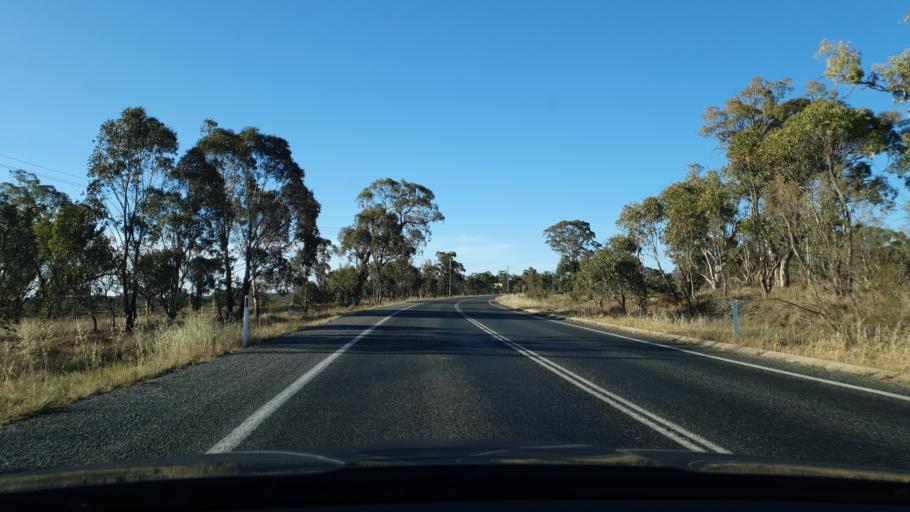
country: AU
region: Queensland
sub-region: Southern Downs
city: Stanthorpe
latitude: -28.6679
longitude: 151.9157
